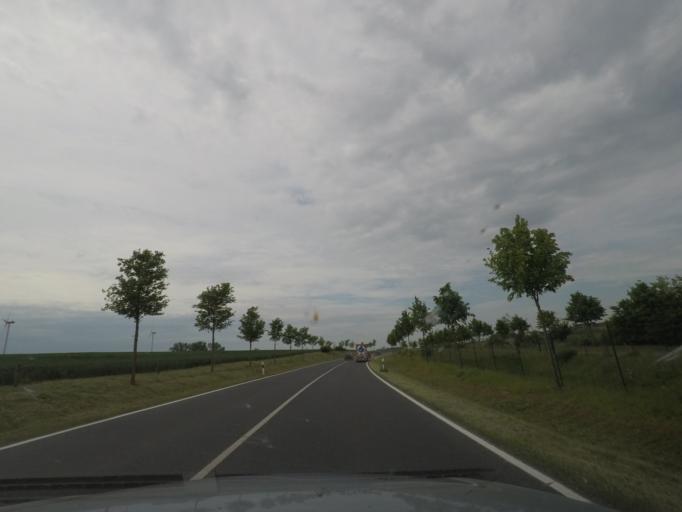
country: DE
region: Brandenburg
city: Grunow
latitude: 53.3399
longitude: 13.9395
